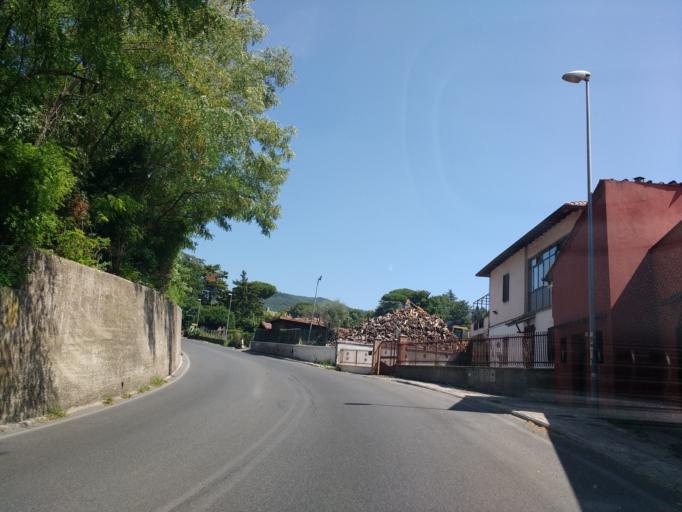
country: IT
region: Latium
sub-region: Citta metropolitana di Roma Capitale
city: Rocca di Papa
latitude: 41.7740
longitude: 12.6929
